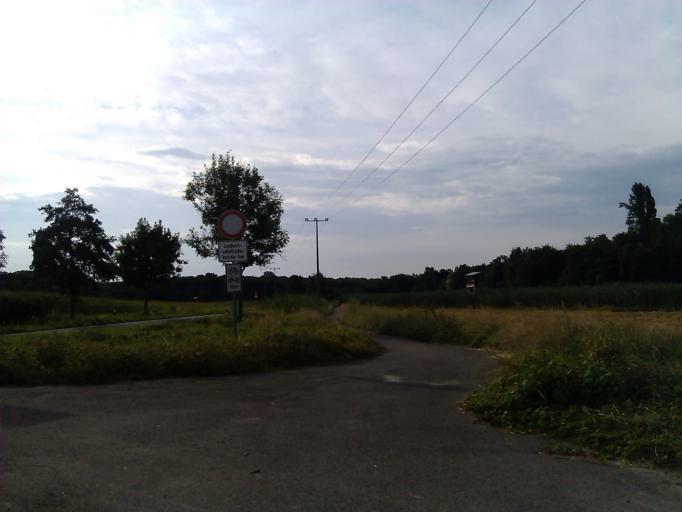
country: DE
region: Rheinland-Pfalz
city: Altrip
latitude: 49.4228
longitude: 8.4795
